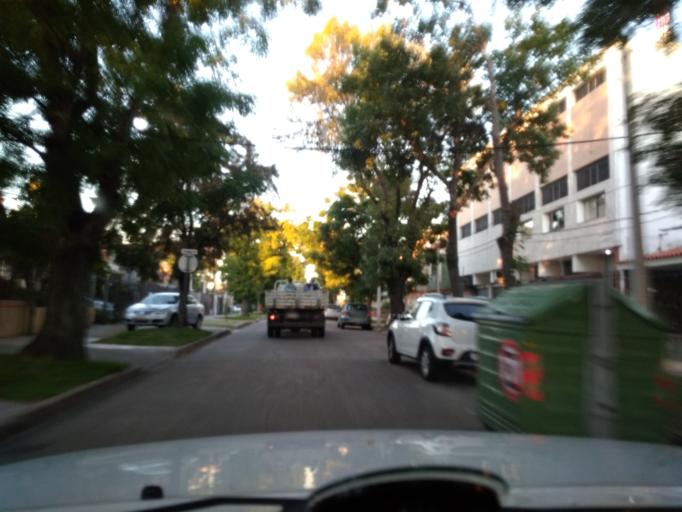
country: UY
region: Canelones
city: Paso de Carrasco
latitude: -34.8912
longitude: -56.1136
